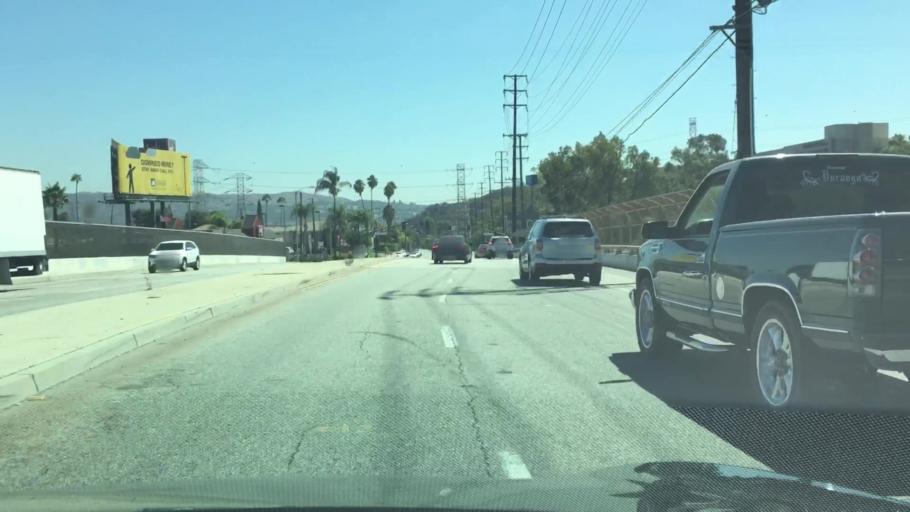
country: US
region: California
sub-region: Los Angeles County
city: South San Gabriel
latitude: 34.0400
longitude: -118.0812
